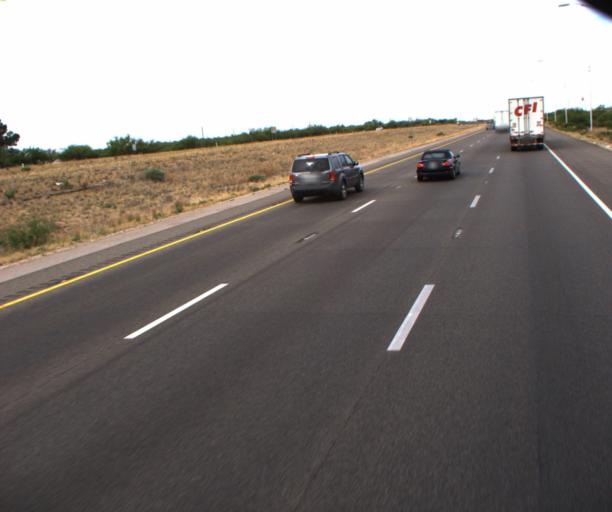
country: US
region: Arizona
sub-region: Cochise County
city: Whetstone
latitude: 31.9635
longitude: -110.3617
